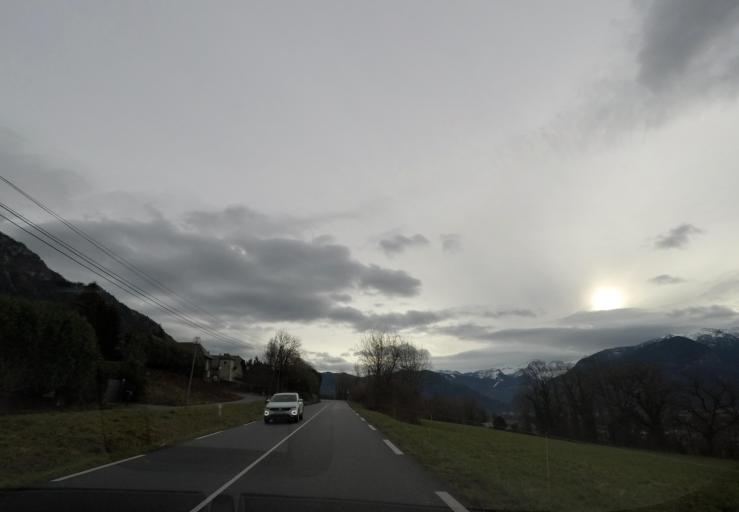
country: FR
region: Rhone-Alpes
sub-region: Departement de la Haute-Savoie
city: Thyez
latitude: 46.0902
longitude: 6.5229
